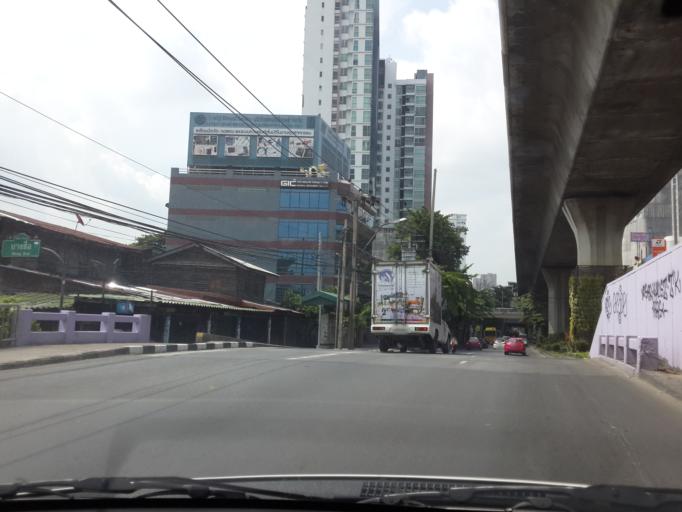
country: TH
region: Bangkok
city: Phaya Thai
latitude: 13.7963
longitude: 100.5507
